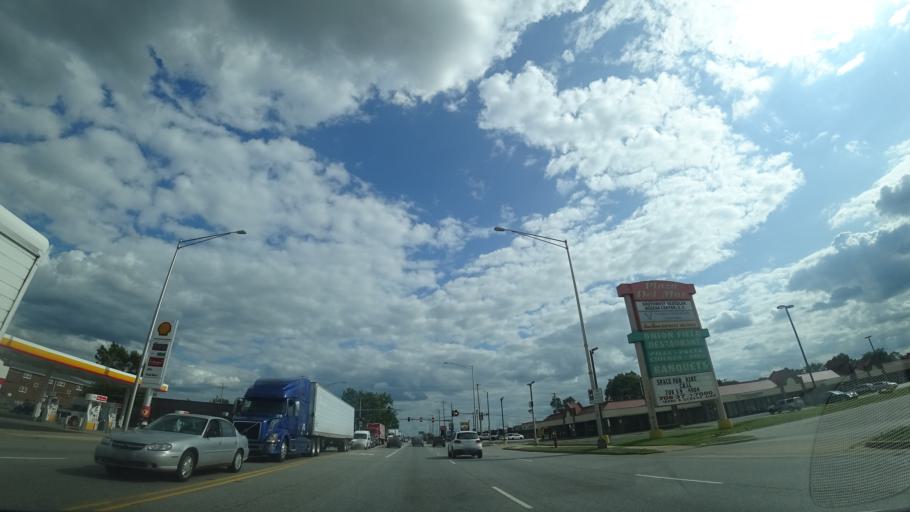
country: US
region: Illinois
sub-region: Cook County
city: Alsip
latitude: 41.6701
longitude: -87.7390
